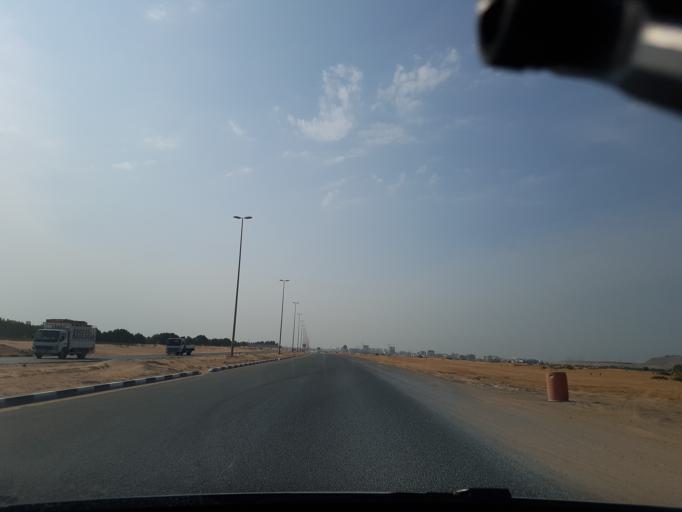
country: AE
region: Ajman
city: Ajman
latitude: 25.4107
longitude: 55.5672
